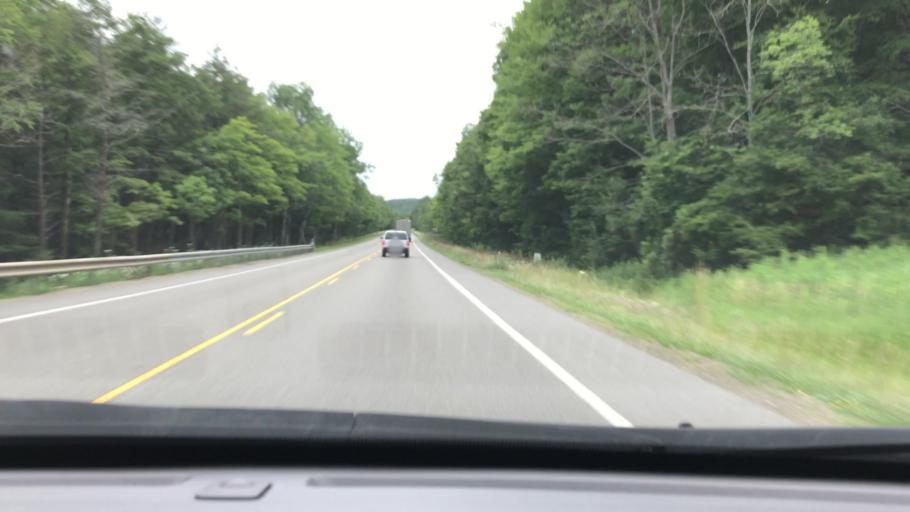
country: US
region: Pennsylvania
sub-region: McKean County
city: Kane
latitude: 41.6785
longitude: -78.6860
